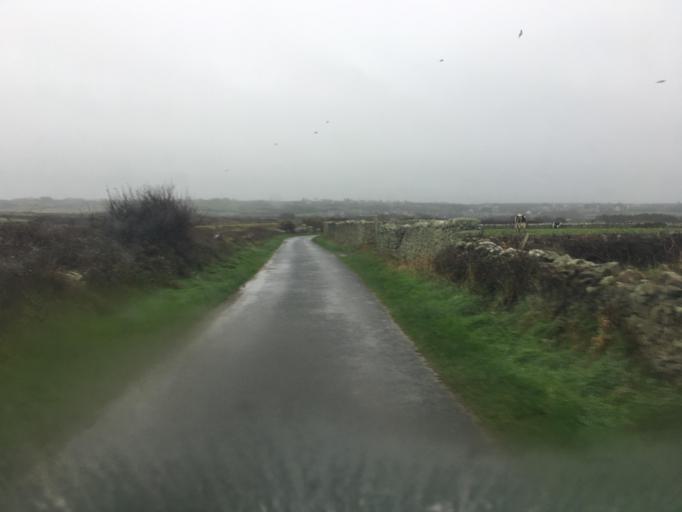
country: FR
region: Lower Normandy
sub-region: Departement de la Manche
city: Beaumont-Hague
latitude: 49.7232
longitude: -1.9232
